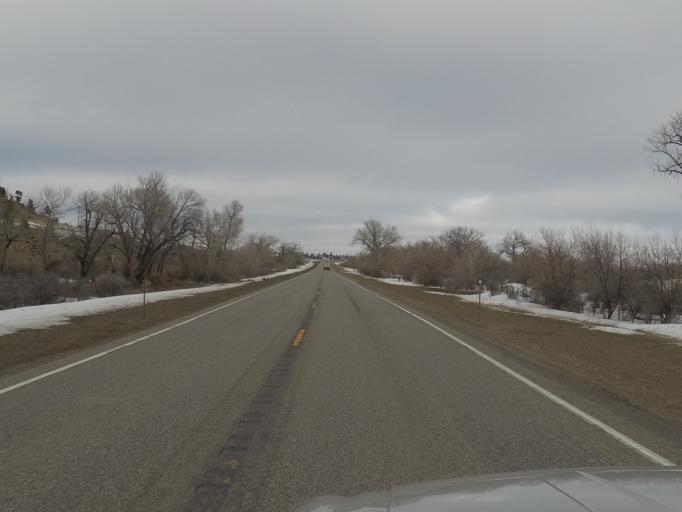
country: US
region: Montana
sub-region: Golden Valley County
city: Ryegate
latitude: 46.3013
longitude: -109.0238
